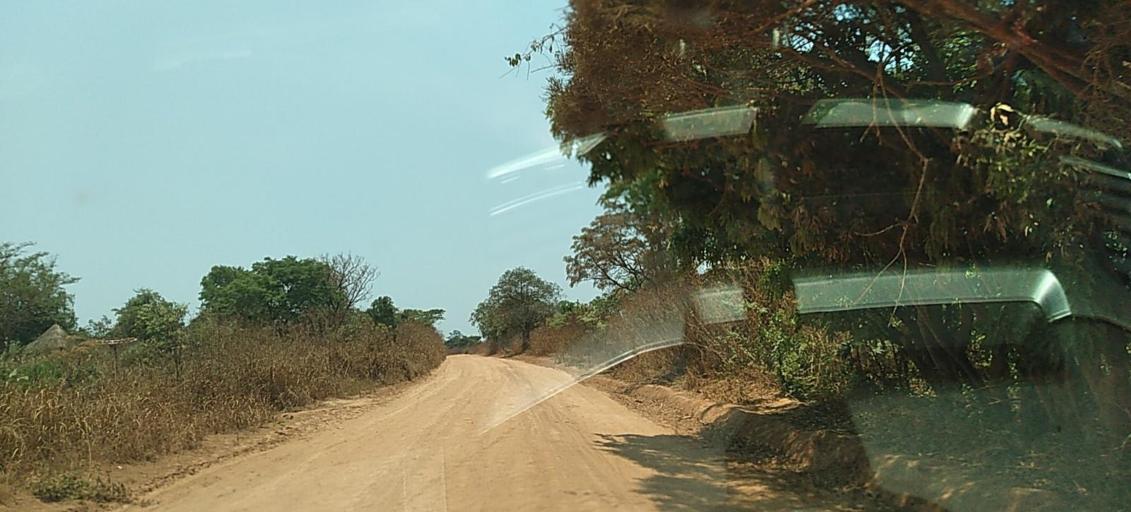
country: CD
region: Katanga
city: Kipushi
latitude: -11.7862
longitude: 27.1711
